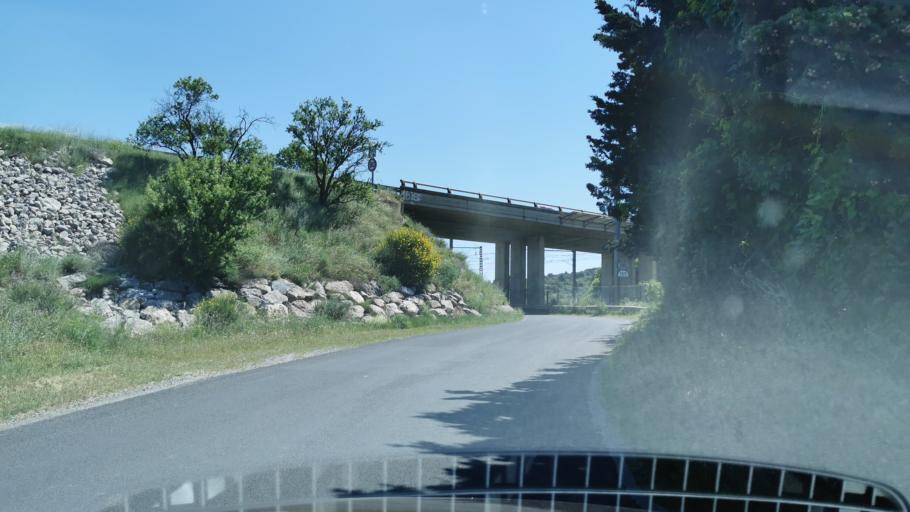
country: FR
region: Languedoc-Roussillon
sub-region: Departement de l'Aude
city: Nevian
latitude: 43.2107
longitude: 2.8744
